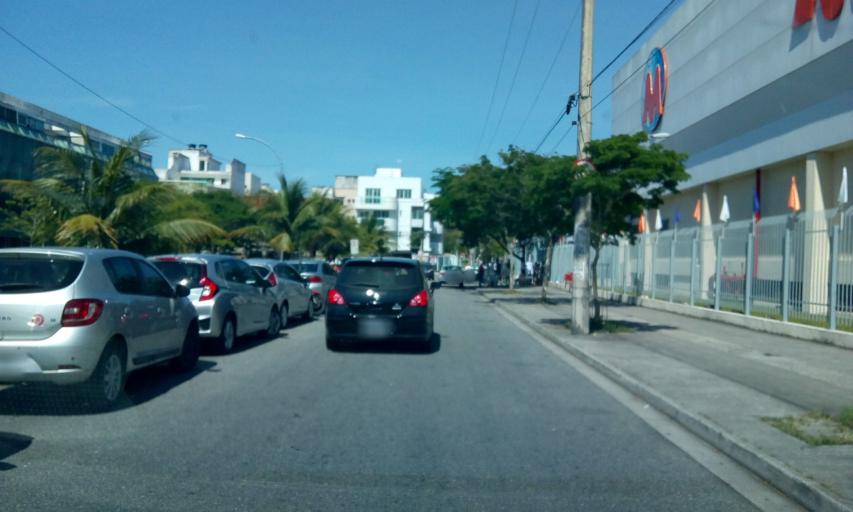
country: BR
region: Rio de Janeiro
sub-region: Nilopolis
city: Nilopolis
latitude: -23.0095
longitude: -43.4426
